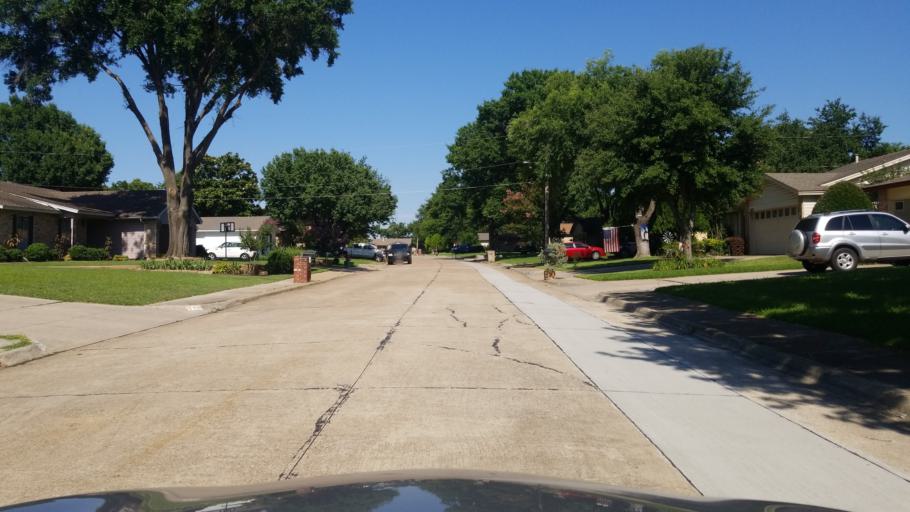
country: US
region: Texas
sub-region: Dallas County
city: Grand Prairie
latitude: 32.6785
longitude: -97.0134
